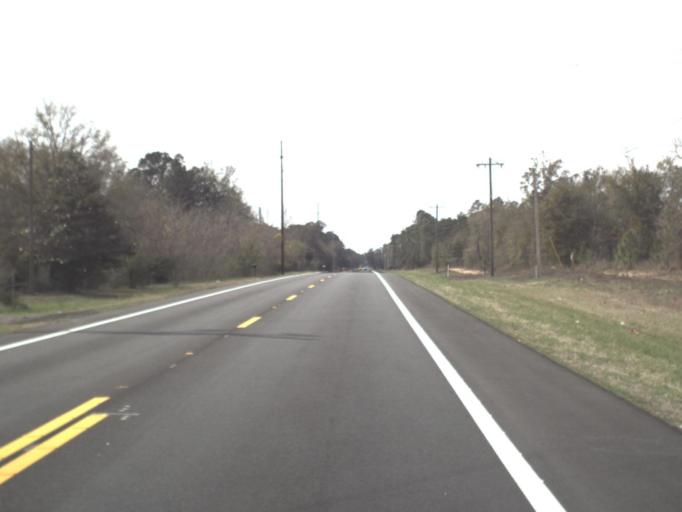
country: US
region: Florida
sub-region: Gadsden County
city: Midway
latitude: 30.4413
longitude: -84.4404
